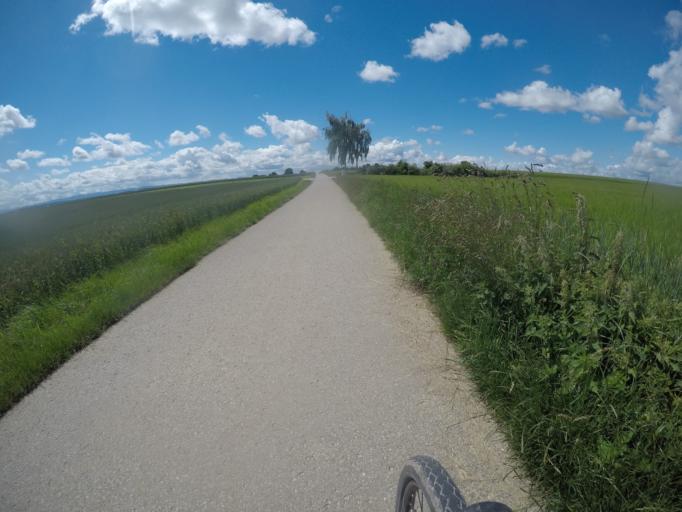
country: DE
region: Baden-Wuerttemberg
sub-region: Regierungsbezirk Stuttgart
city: Motzingen
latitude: 48.4891
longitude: 8.7499
